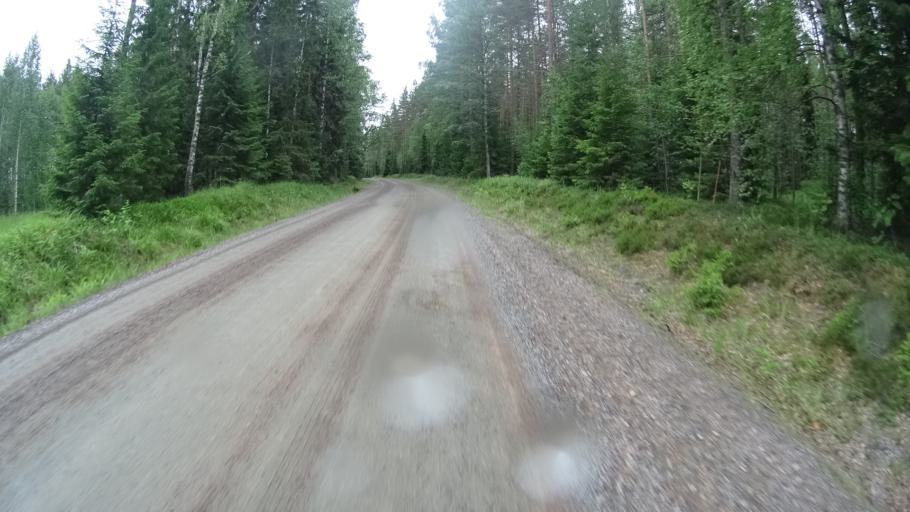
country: FI
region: Uusimaa
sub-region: Helsinki
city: Karkkila
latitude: 60.5962
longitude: 24.1893
